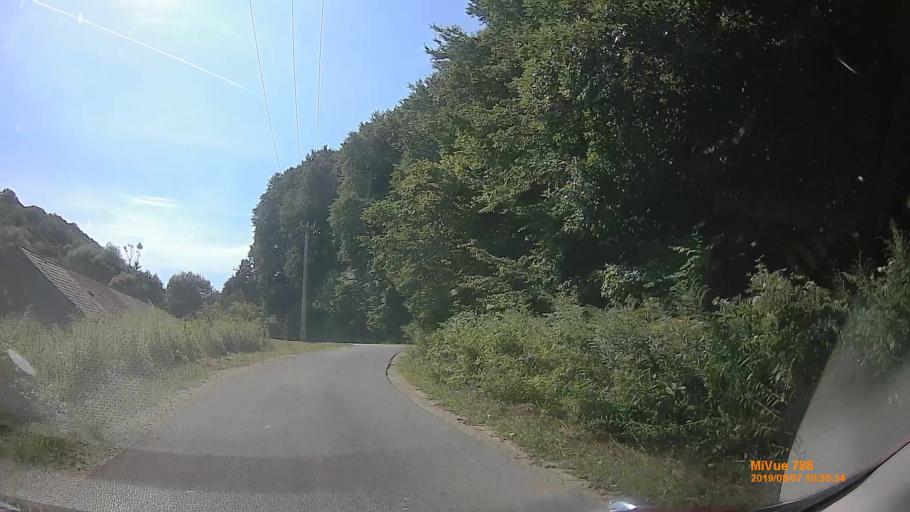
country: HU
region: Veszprem
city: Ajka
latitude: 47.0755
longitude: 17.5793
